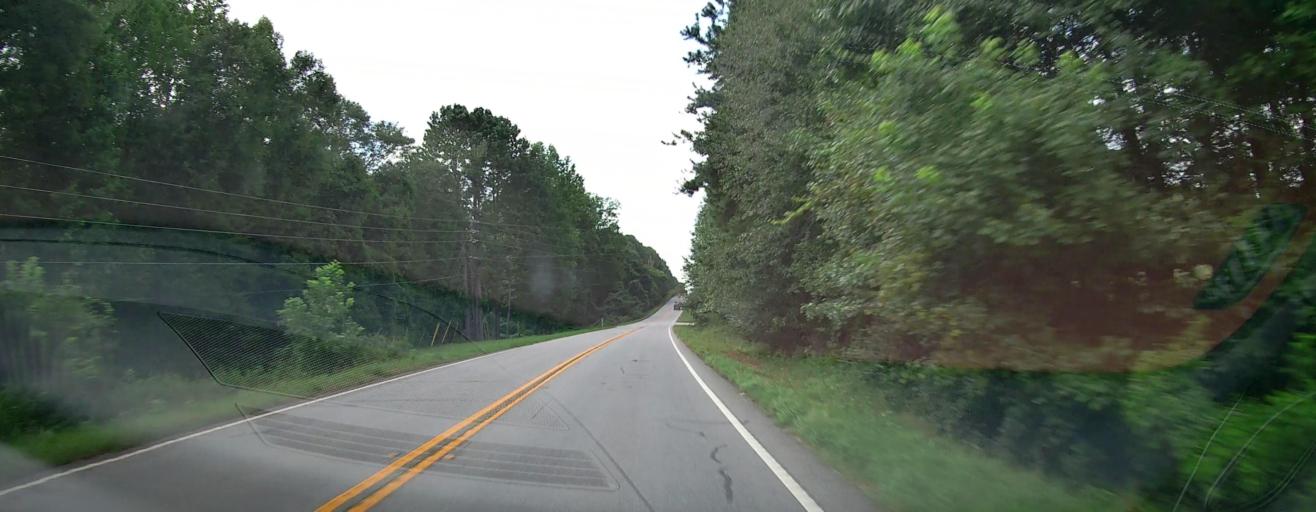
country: US
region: Georgia
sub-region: Meriwether County
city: Greenville
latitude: 33.0677
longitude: -84.5719
